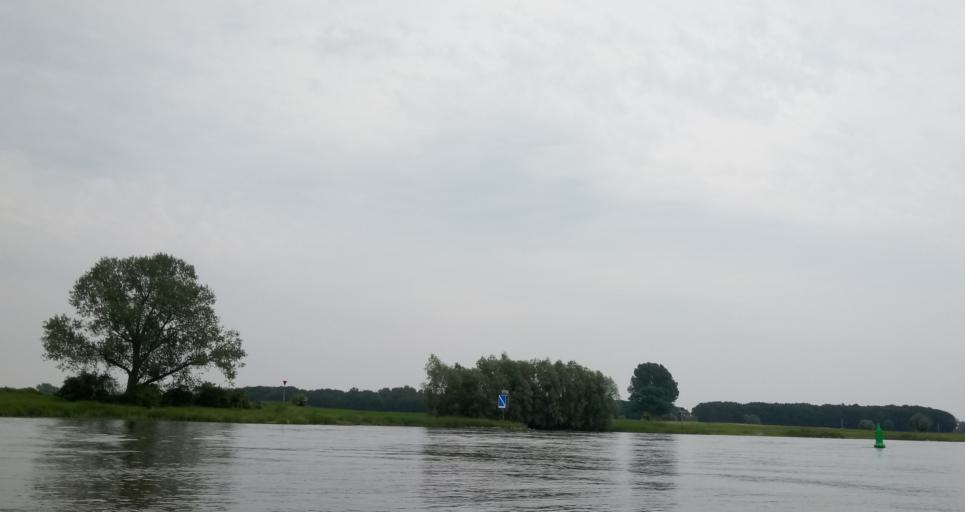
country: NL
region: Gelderland
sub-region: Gemeente Voorst
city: Voorst
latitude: 52.1893
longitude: 6.1673
